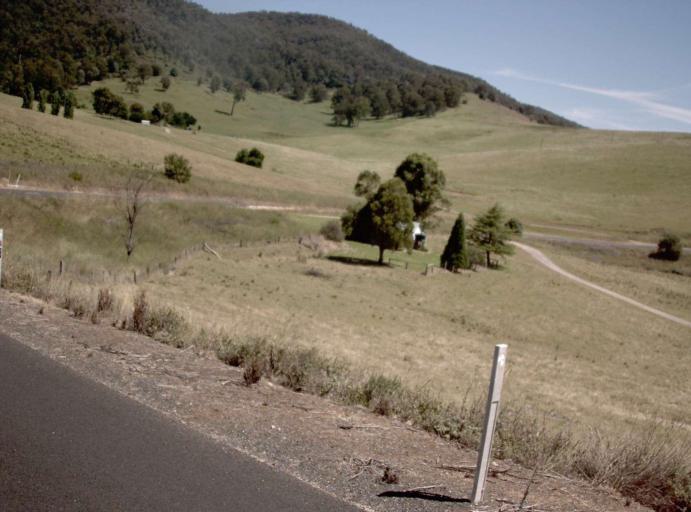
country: AU
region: Victoria
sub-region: East Gippsland
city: Lakes Entrance
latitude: -37.4148
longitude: 148.2057
